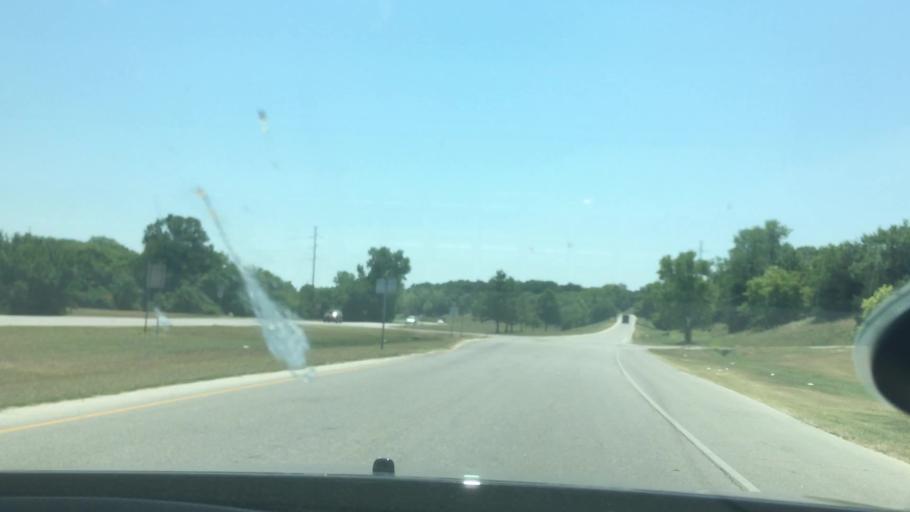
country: US
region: Oklahoma
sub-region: Pontotoc County
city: Ada
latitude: 34.7535
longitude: -96.6581
